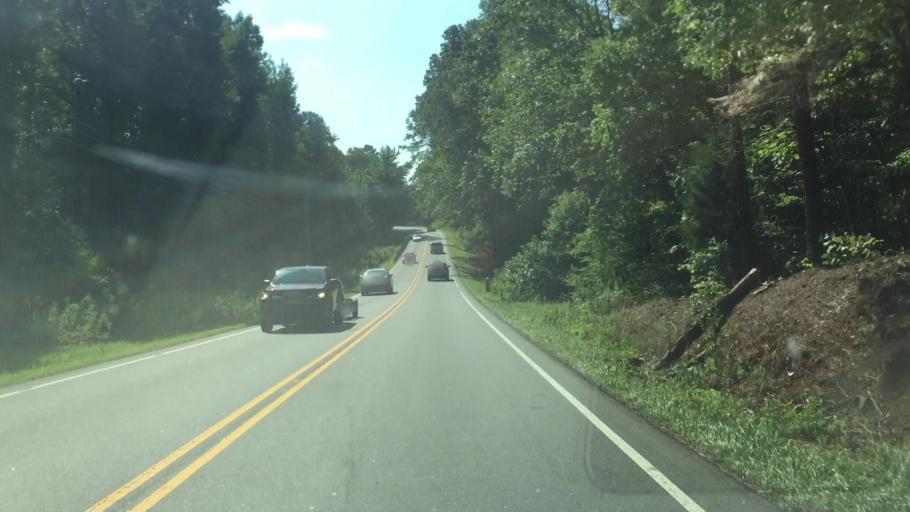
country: US
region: North Carolina
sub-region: Union County
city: Fairview
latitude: 35.1641
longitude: -80.5872
